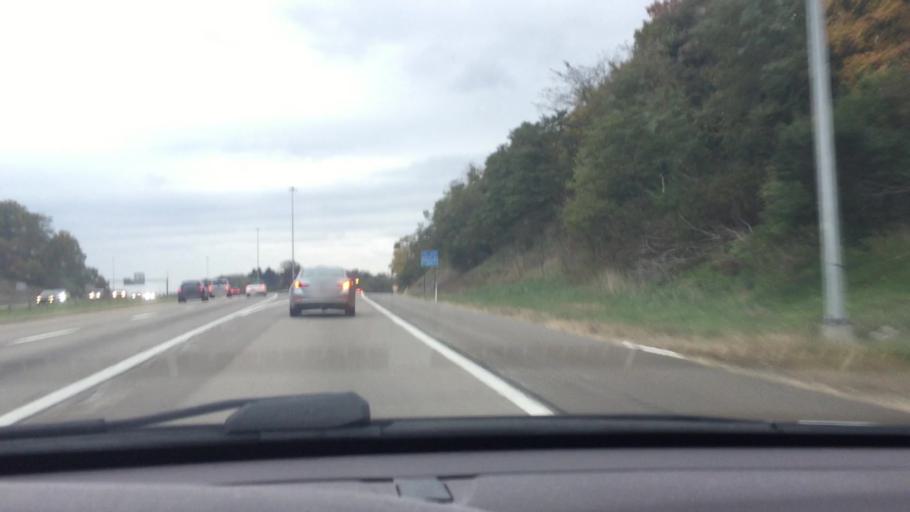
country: US
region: Pennsylvania
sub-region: Allegheny County
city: Ingram
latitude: 40.4460
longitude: -80.1107
